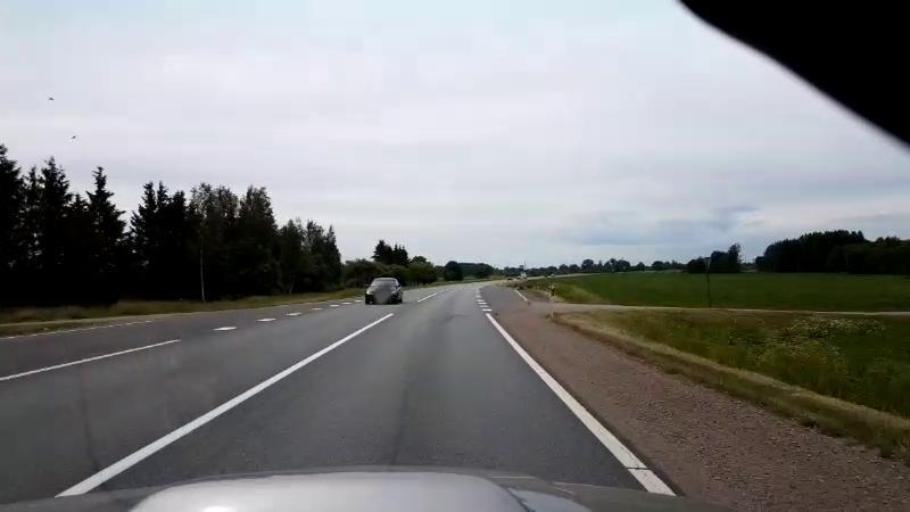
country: LV
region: Bauskas Rajons
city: Bauska
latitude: 56.4836
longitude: 24.1768
